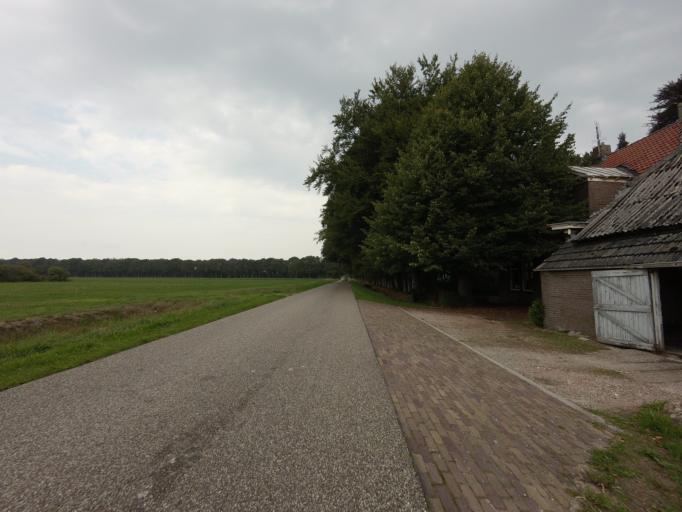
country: NL
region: Drenthe
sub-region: Gemeente Tynaarlo
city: Vries
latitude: 53.0572
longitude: 6.5876
